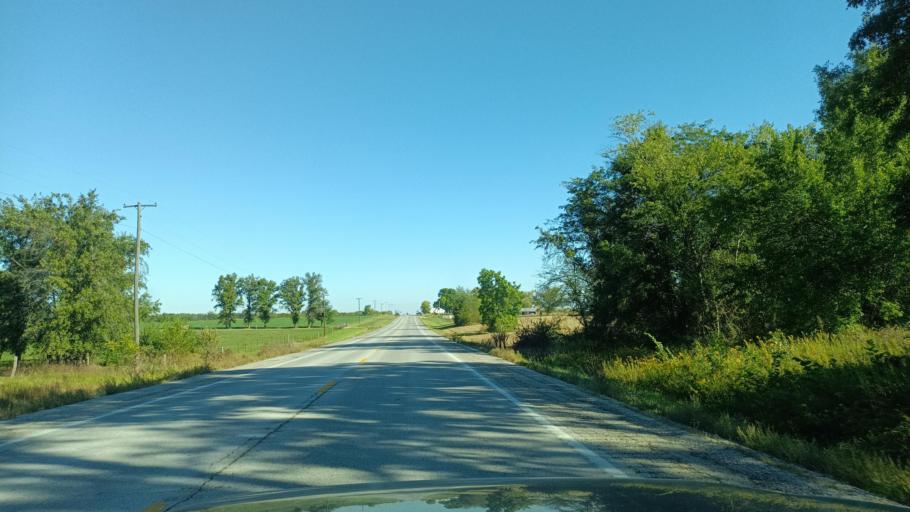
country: US
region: Missouri
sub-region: Audrain County
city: Vandalia
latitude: 39.3475
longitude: -91.6428
